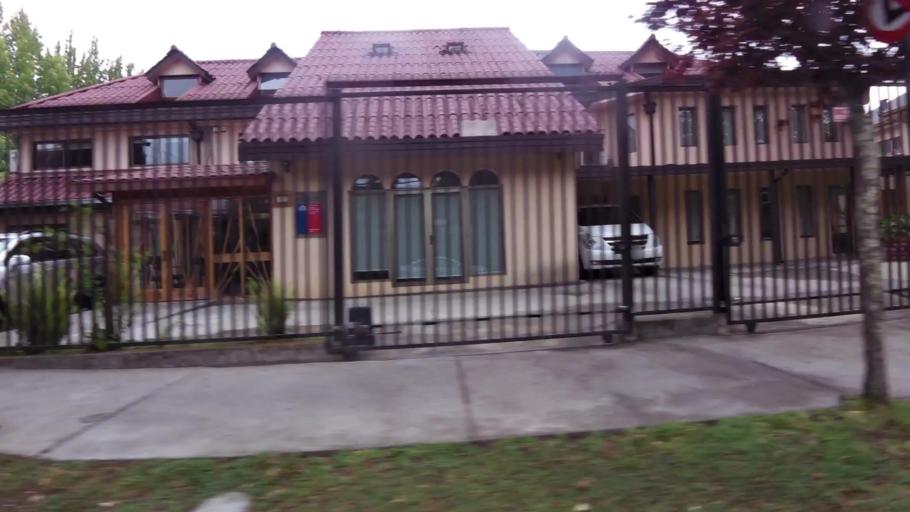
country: CL
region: Biobio
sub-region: Provincia de Concepcion
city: Concepcion
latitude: -36.8306
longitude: -73.0393
